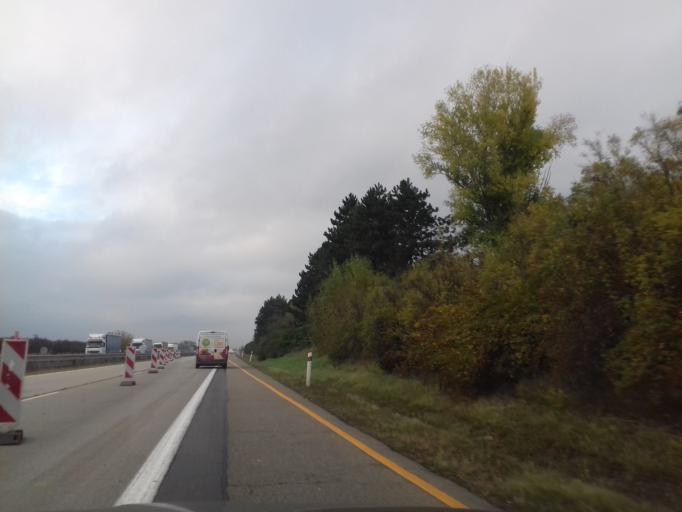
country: CZ
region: South Moravian
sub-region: Okres Brno-Venkov
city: Blucina
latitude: 49.0772
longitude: 16.6606
